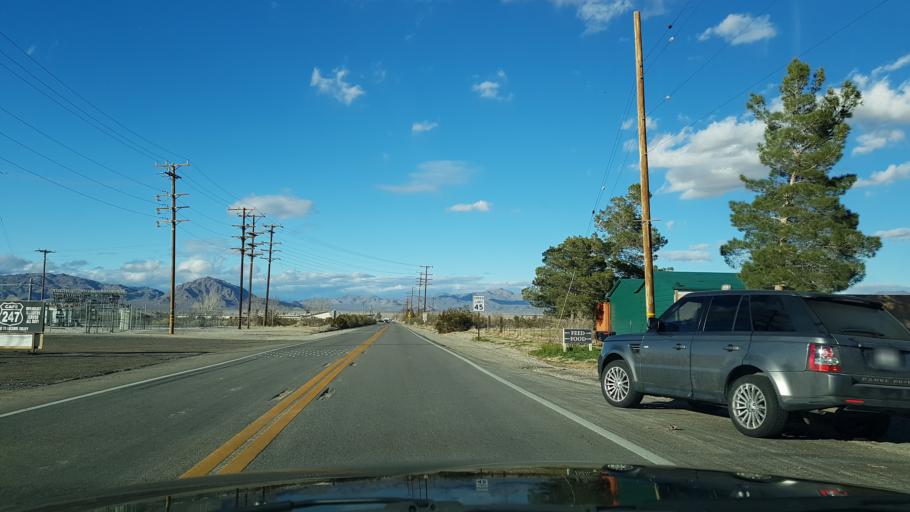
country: US
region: California
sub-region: San Bernardino County
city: Lucerne Valley
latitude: 34.4442
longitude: -116.9459
